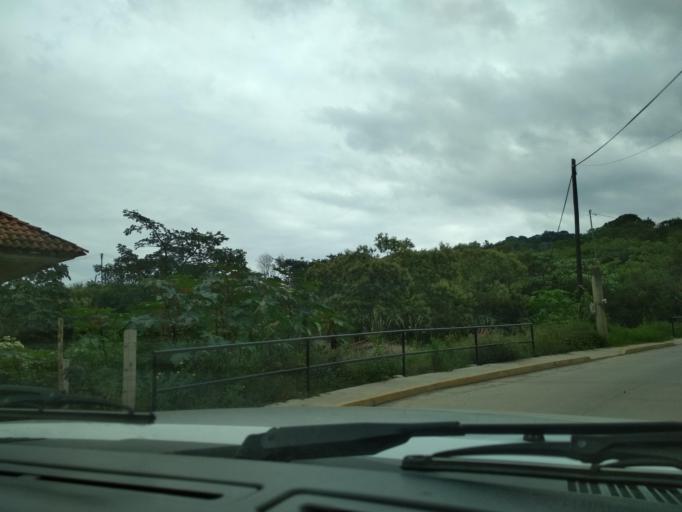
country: MX
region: Veracruz
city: El Castillo
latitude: 19.5849
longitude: -96.8724
